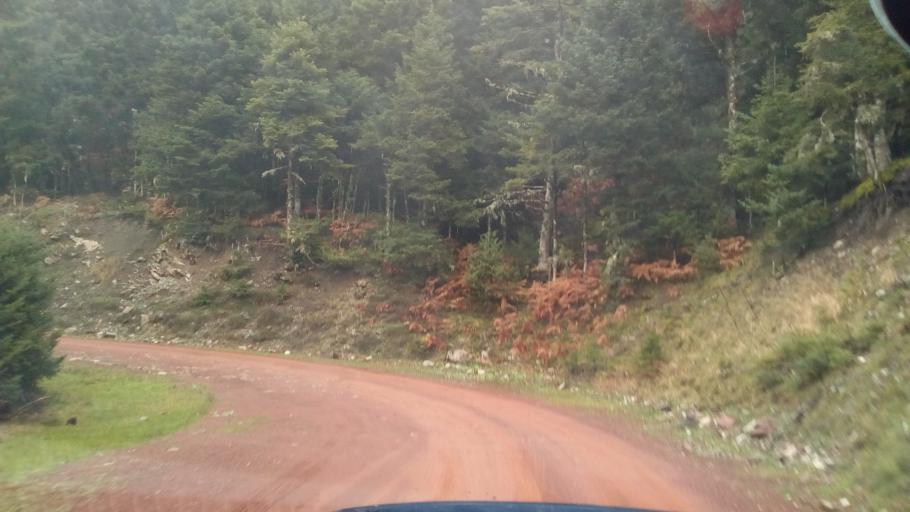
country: GR
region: West Greece
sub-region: Nomos Aitolias kai Akarnanias
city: Nafpaktos
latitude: 38.5379
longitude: 21.8605
